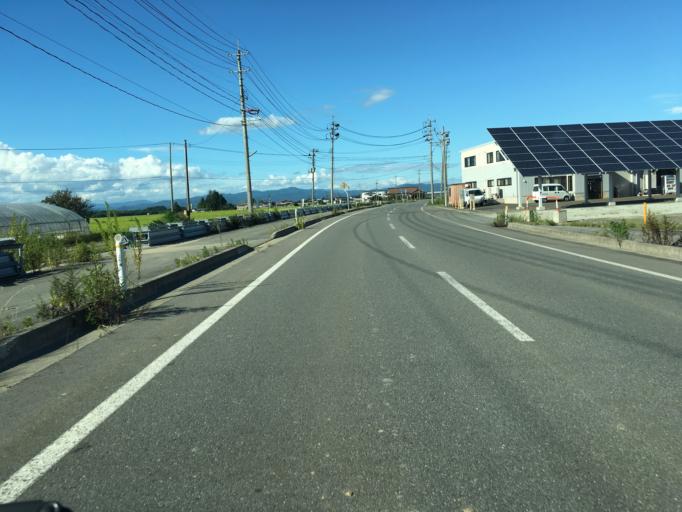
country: JP
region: Yamagata
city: Yonezawa
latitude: 37.9482
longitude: 140.1071
